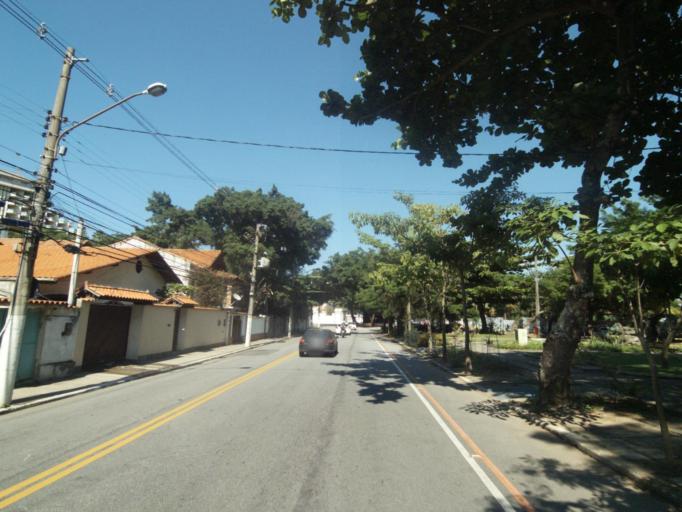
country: BR
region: Rio de Janeiro
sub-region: Niteroi
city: Niteroi
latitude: -22.9019
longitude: -43.1343
